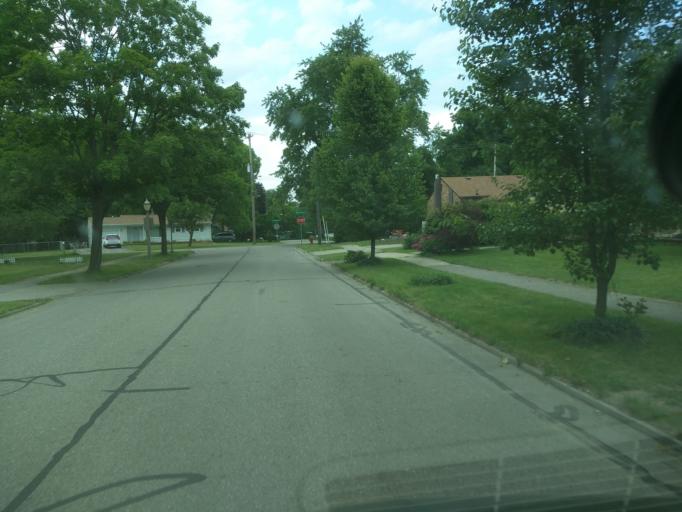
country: US
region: Michigan
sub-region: Ingham County
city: Edgemont Park
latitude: 42.7610
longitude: -84.5868
